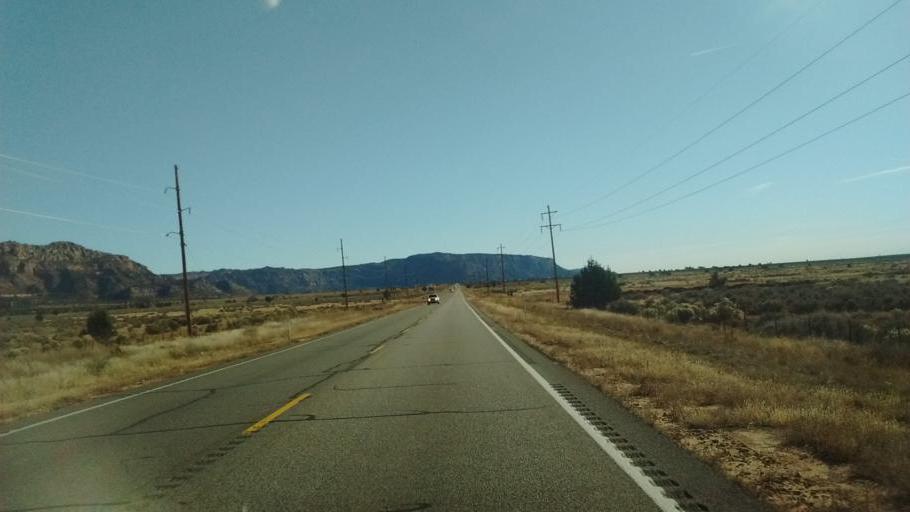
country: US
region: Arizona
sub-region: Mohave County
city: Colorado City
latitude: 37.0181
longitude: -113.0310
